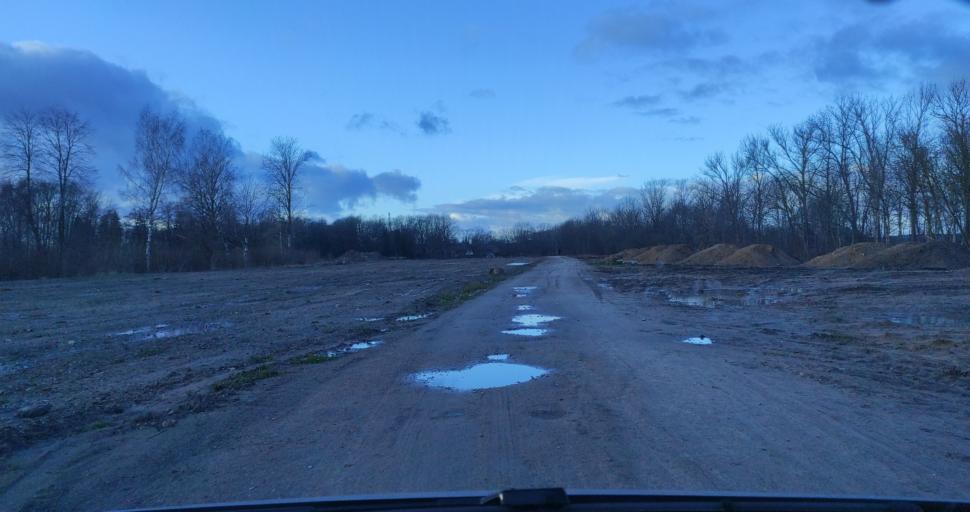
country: LV
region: Kuldigas Rajons
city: Kuldiga
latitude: 56.9652
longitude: 21.9834
